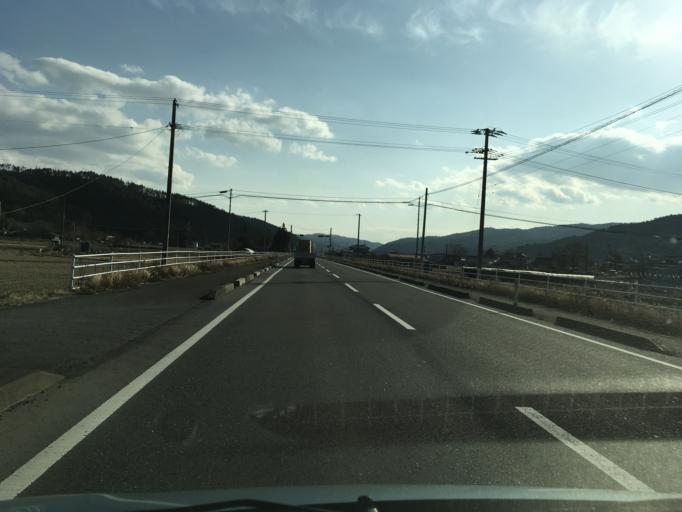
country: JP
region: Iwate
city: Ichinoseki
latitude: 38.7739
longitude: 141.3364
